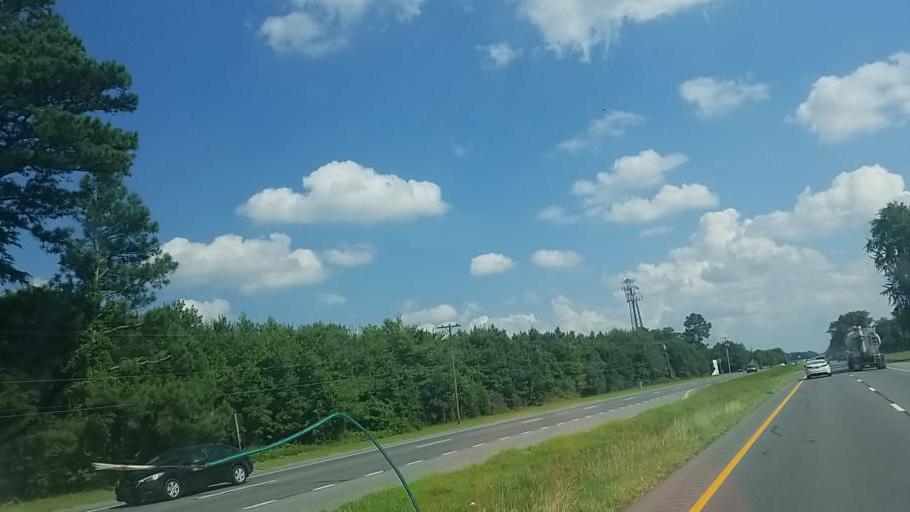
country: US
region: Delaware
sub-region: Sussex County
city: Georgetown
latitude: 38.6324
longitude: -75.3487
